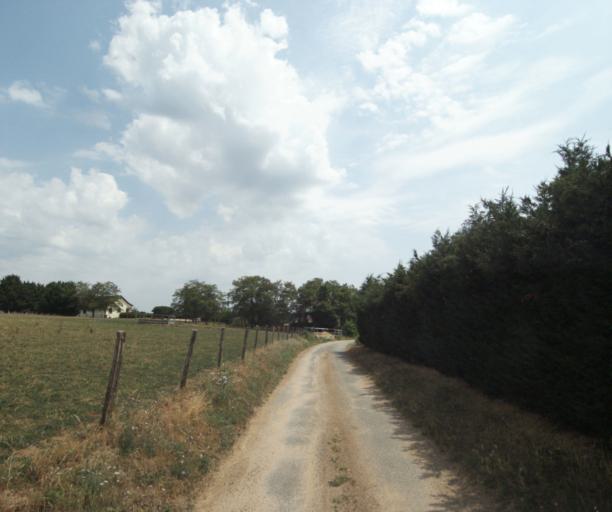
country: FR
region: Bourgogne
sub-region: Departement de Saone-et-Loire
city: Gueugnon
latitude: 46.5909
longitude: 4.0231
